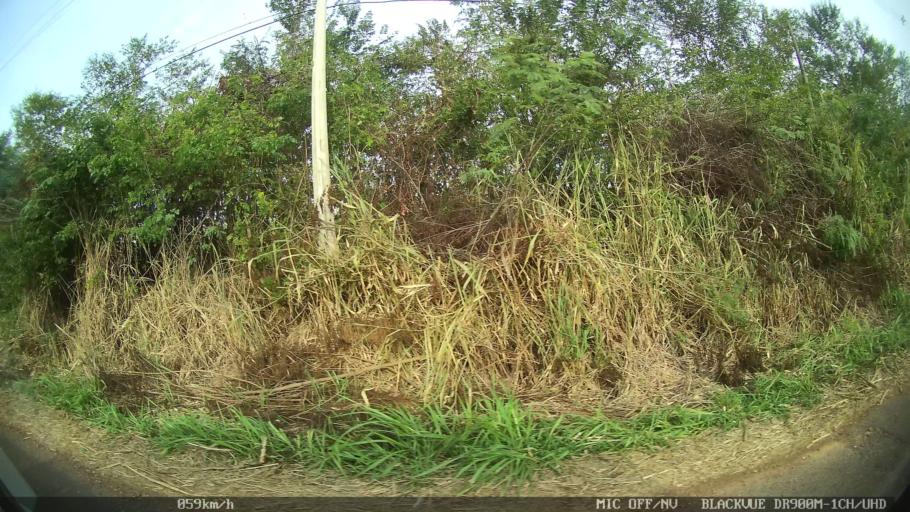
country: BR
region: Sao Paulo
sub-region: Piracicaba
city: Piracicaba
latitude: -22.6954
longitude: -47.5854
